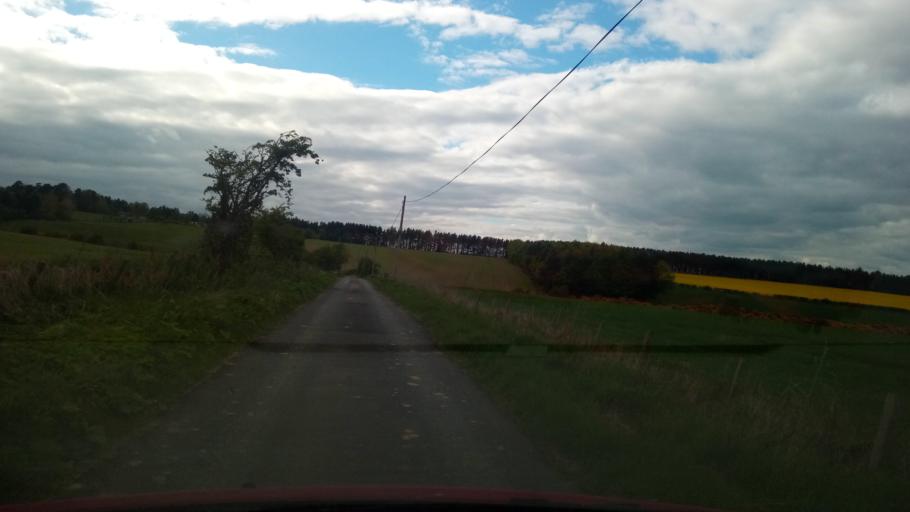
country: GB
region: Scotland
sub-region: The Scottish Borders
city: Saint Boswells
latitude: 55.5075
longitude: -2.6426
